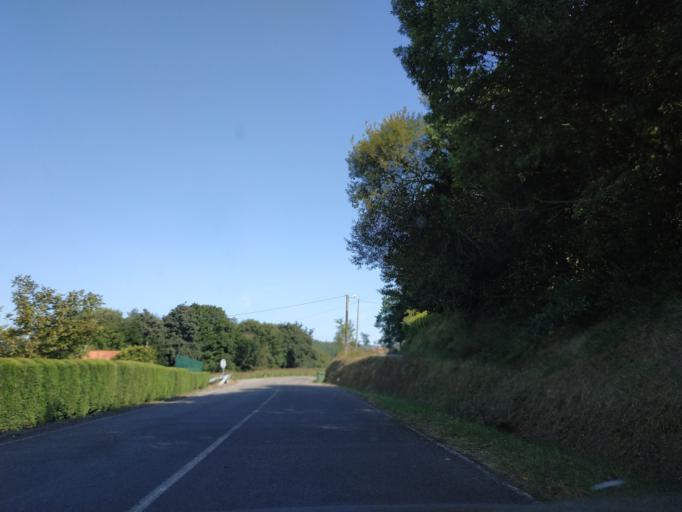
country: ES
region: Galicia
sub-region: Provincia da Coruna
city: Laracha
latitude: 43.2280
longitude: -8.5522
